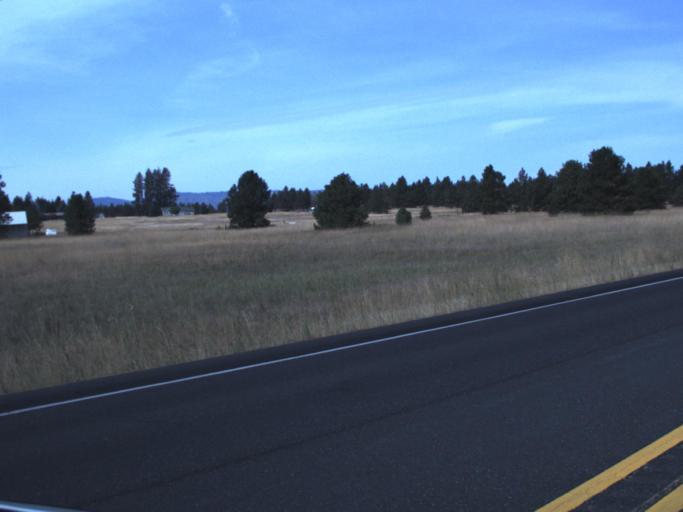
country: US
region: Washington
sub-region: Spokane County
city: Deer Park
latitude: 47.9335
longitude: -117.4684
